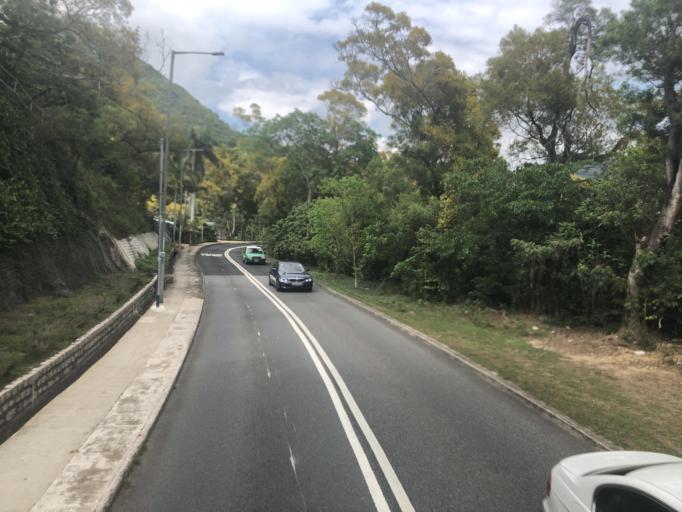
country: HK
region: Sai Kung
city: Sai Kung
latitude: 22.3899
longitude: 114.2949
